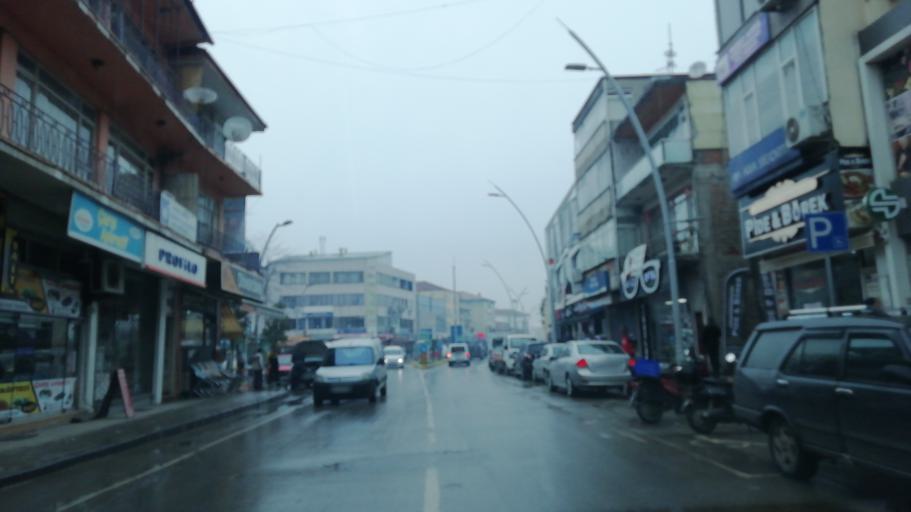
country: TR
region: Sakarya
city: Akyazi
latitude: 40.6827
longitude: 30.6251
